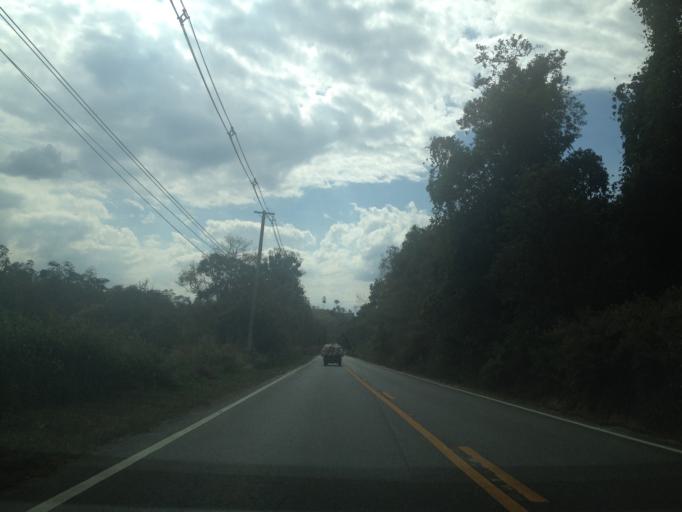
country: TH
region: Mae Hong Son
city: Pa Pae
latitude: 18.1614
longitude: 98.2214
